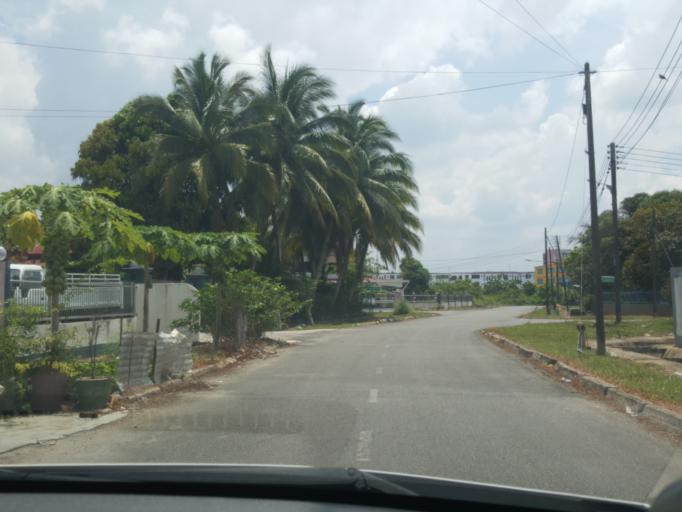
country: MY
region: Sarawak
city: Sarikei
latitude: 2.1254
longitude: 111.5221
